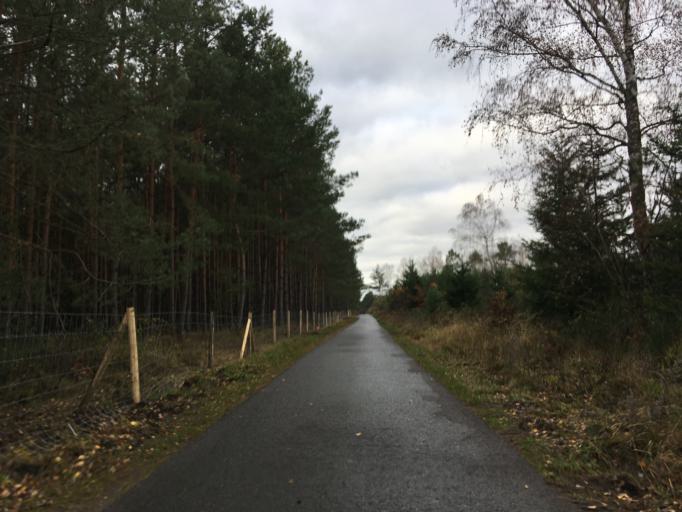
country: DE
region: Brandenburg
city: Jamlitz
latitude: 52.0184
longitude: 14.4824
